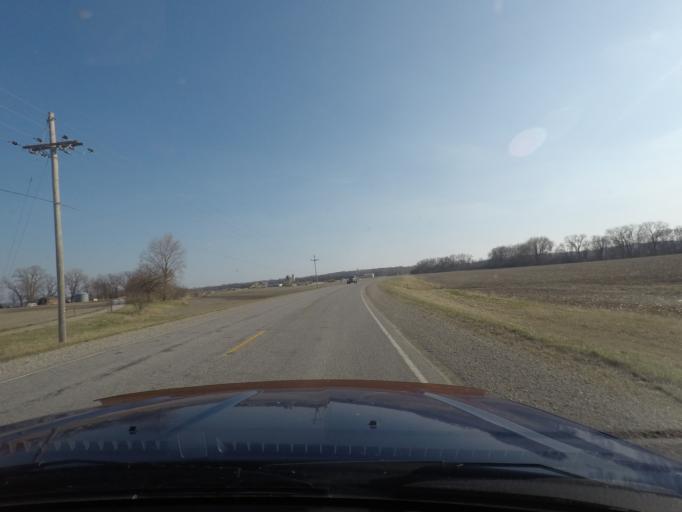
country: US
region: Kansas
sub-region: Jefferson County
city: Oskaloosa
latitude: 39.0618
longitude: -95.3820
